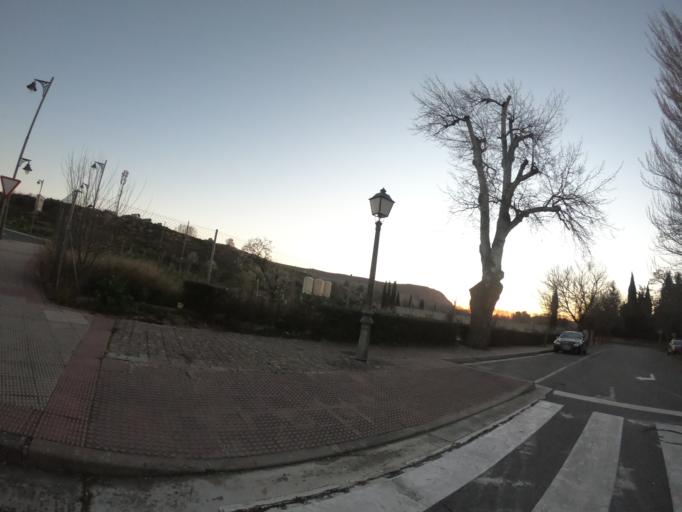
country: ES
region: La Rioja
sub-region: Provincia de La Rioja
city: Logrono
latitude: 42.4754
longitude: -2.4445
